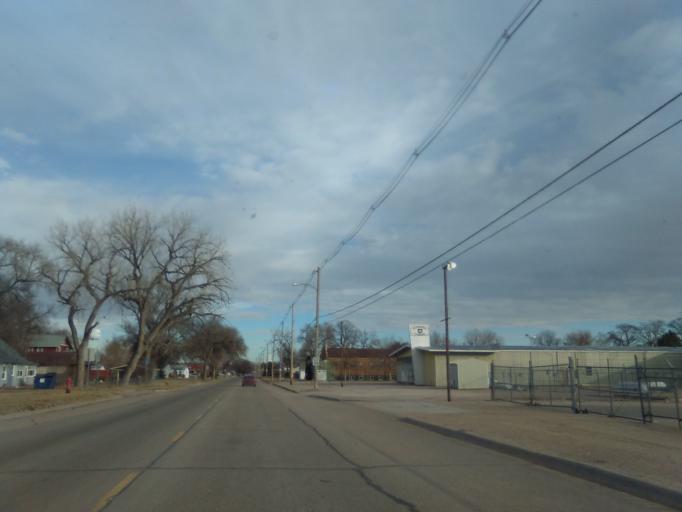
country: US
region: Nebraska
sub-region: Morrill County
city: Bridgeport
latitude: 41.6704
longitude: -103.1051
